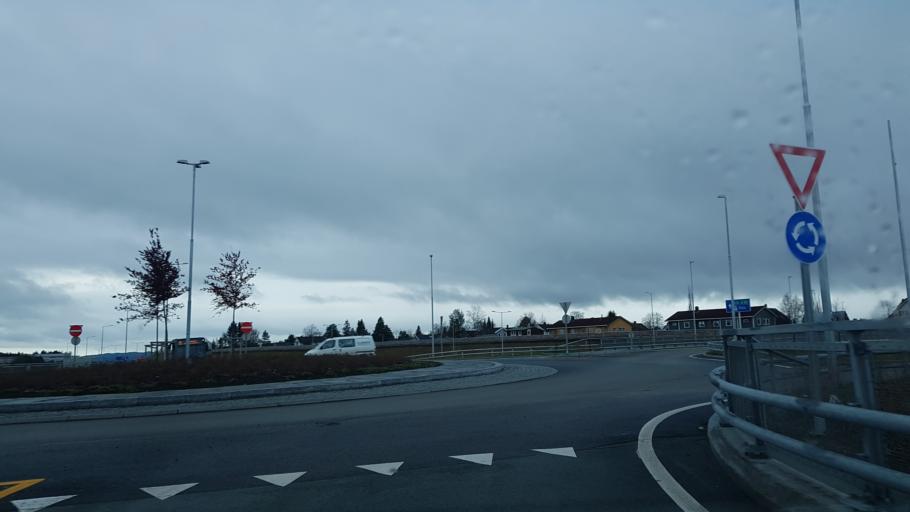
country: NO
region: Sor-Trondelag
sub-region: Trondheim
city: Trondheim
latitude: 63.3467
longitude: 10.3716
